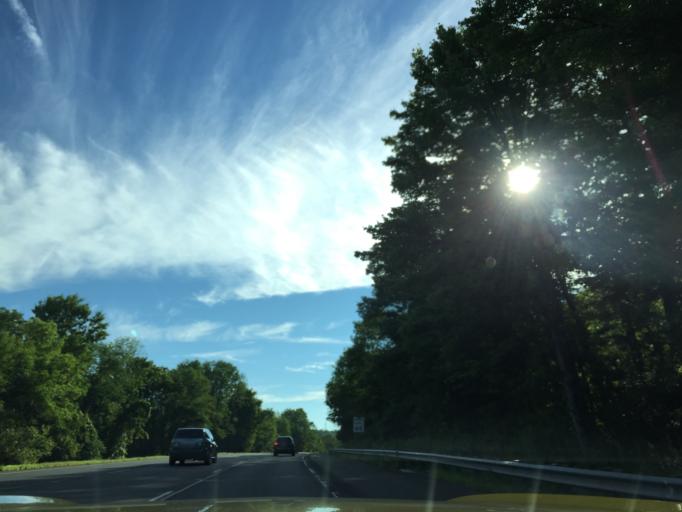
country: US
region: New Jersey
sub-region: Union County
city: Berkeley Heights
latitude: 40.6609
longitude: -74.4346
